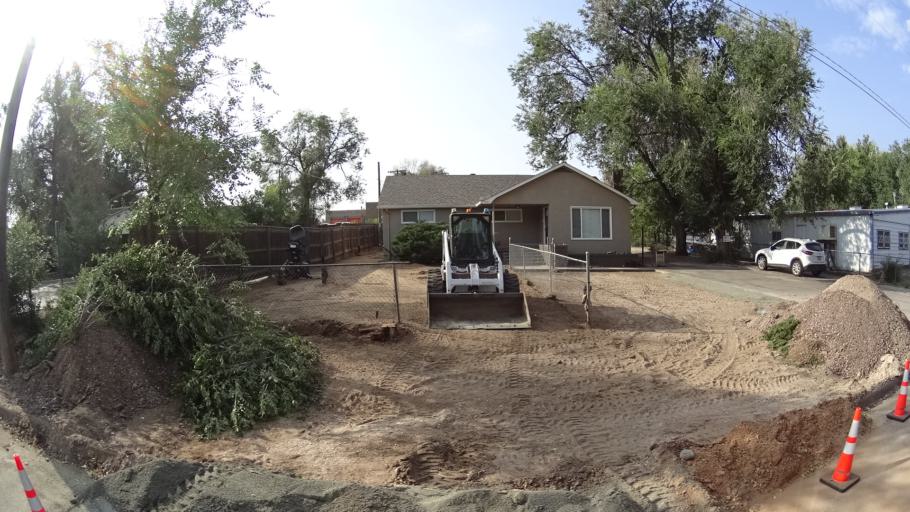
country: US
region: Colorado
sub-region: El Paso County
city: Colorado Springs
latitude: 38.8398
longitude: -104.7817
